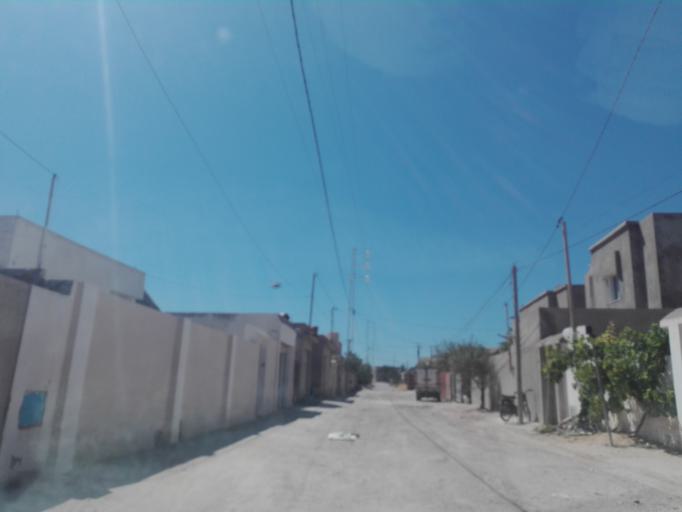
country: TN
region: Safaqis
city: Jabinyanah
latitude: 34.7420
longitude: 11.2979
